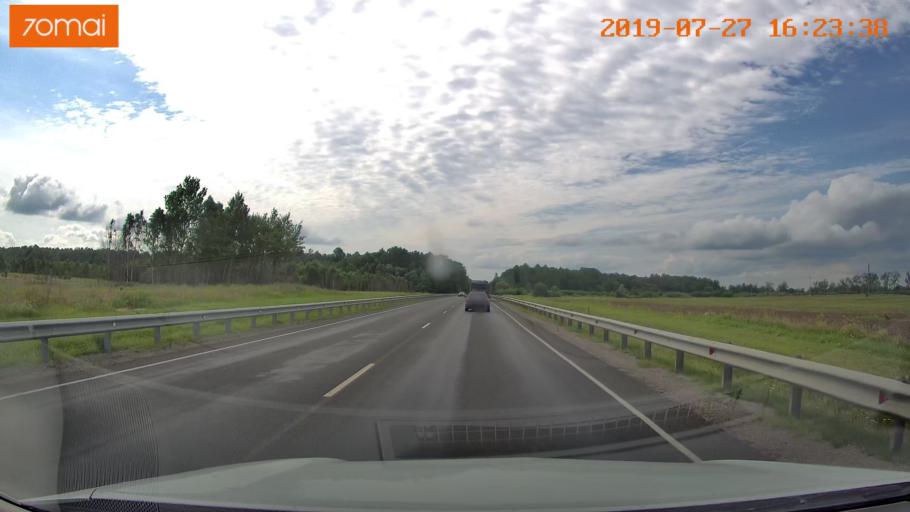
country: RU
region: Kaliningrad
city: Zheleznodorozhnyy
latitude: 54.6316
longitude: 21.4697
